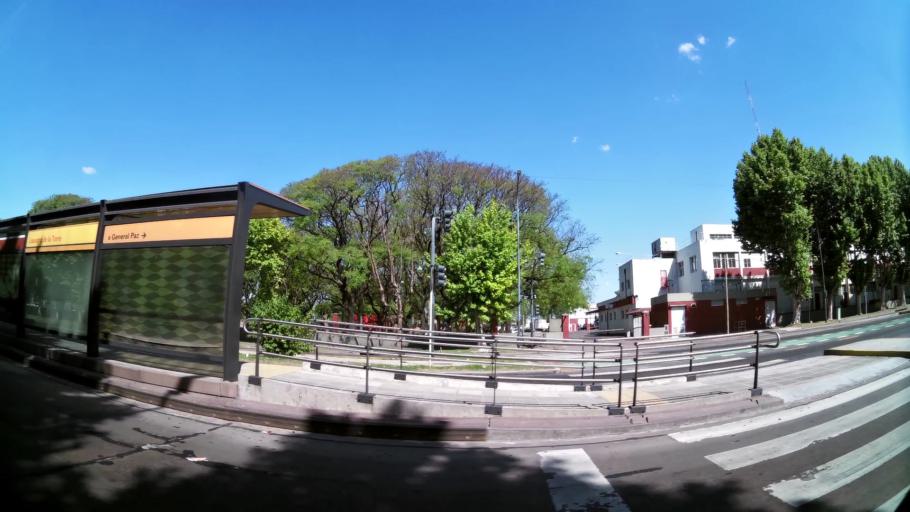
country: AR
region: Buenos Aires F.D.
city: Villa Lugano
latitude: -34.6917
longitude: -58.4633
